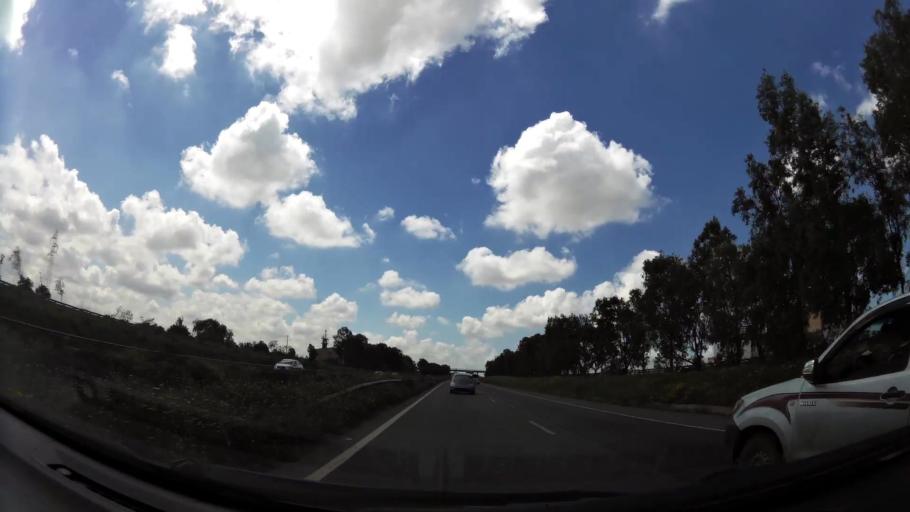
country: MA
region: Grand Casablanca
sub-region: Casablanca
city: Casablanca
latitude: 33.5203
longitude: -7.5791
